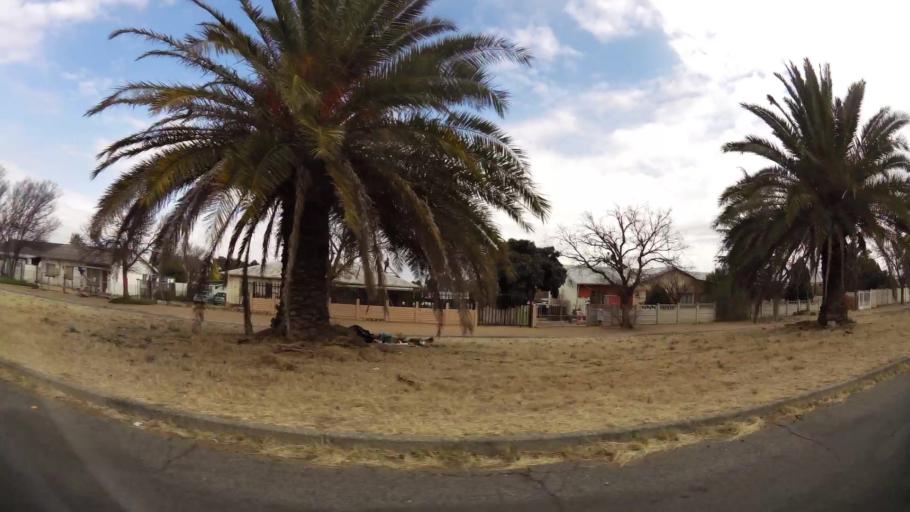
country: ZA
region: Orange Free State
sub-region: Fezile Dabi District Municipality
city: Kroonstad
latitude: -27.6456
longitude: 27.2288
